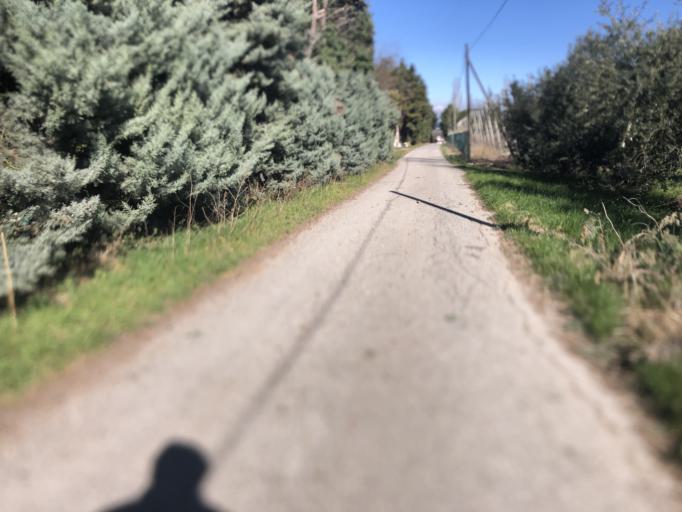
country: IT
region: Veneto
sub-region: Provincia di Verona
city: Sona
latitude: 45.4371
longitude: 10.8156
